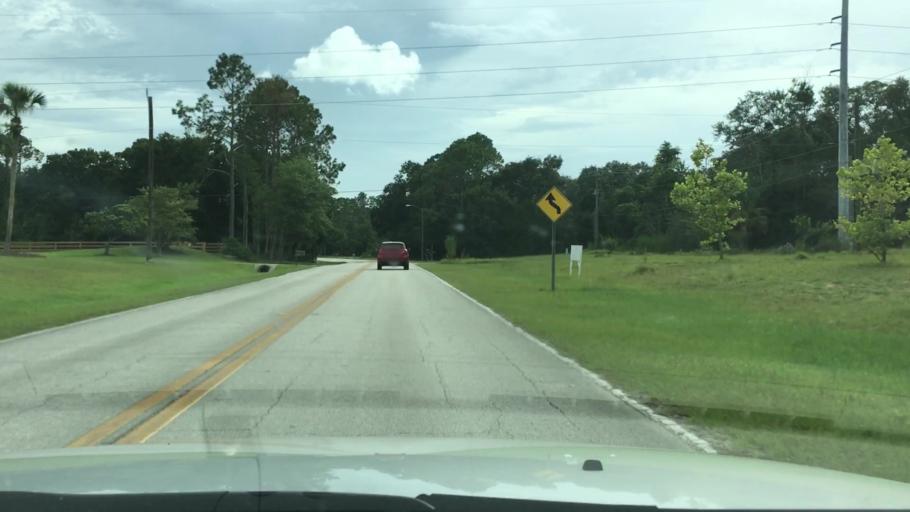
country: US
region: Florida
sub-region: Volusia County
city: Ormond-by-the-Sea
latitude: 29.3344
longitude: -81.1110
